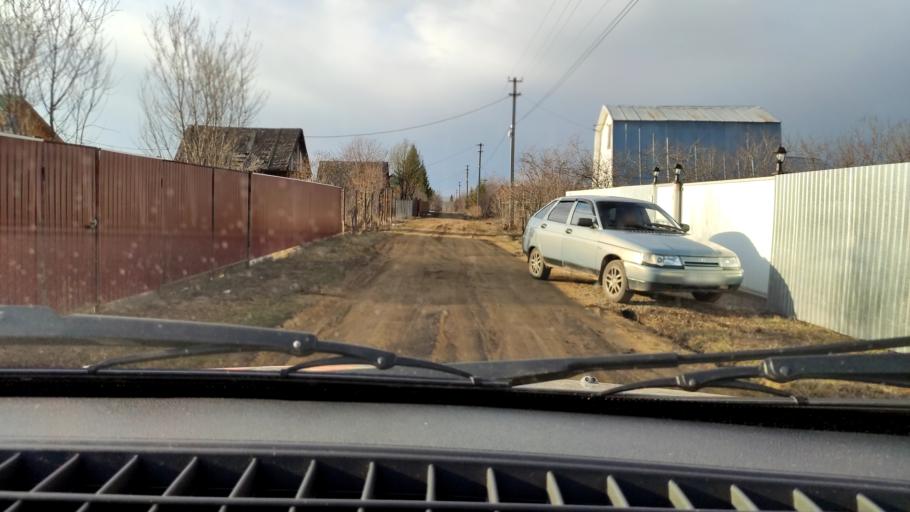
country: RU
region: Bashkortostan
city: Iglino
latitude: 54.8411
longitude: 56.4724
